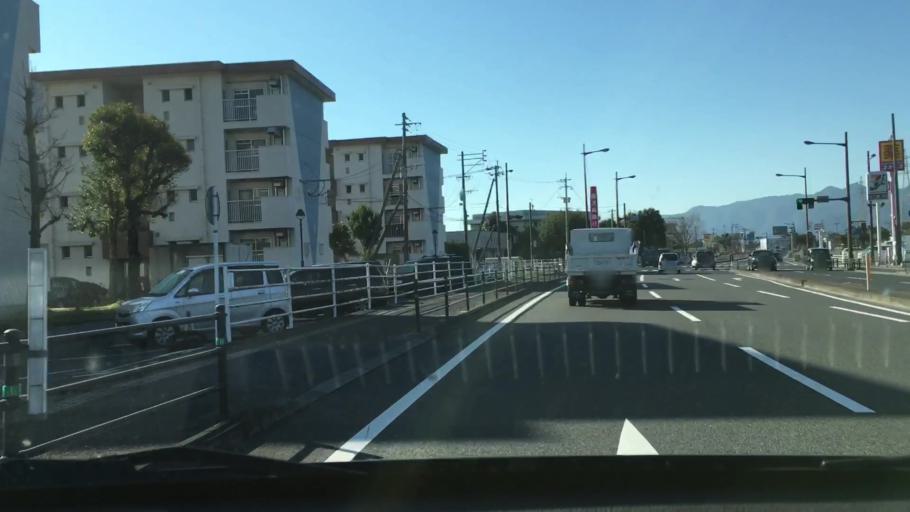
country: JP
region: Kagoshima
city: Kajiki
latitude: 31.7397
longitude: 130.6518
